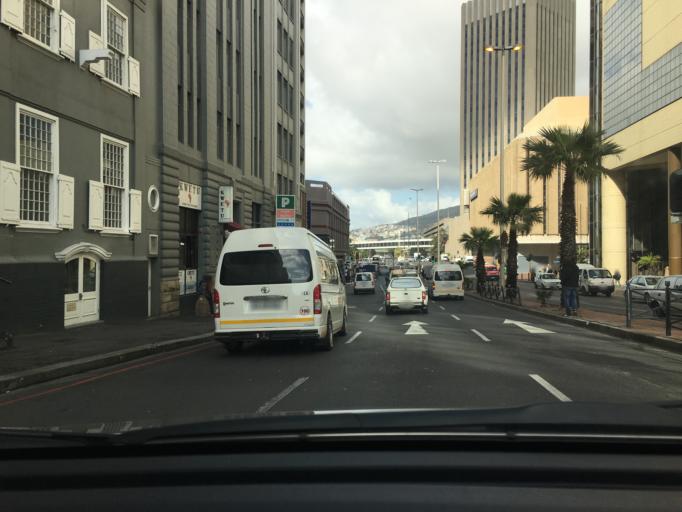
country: ZA
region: Western Cape
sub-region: City of Cape Town
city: Cape Town
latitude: -33.9210
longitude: 18.4218
